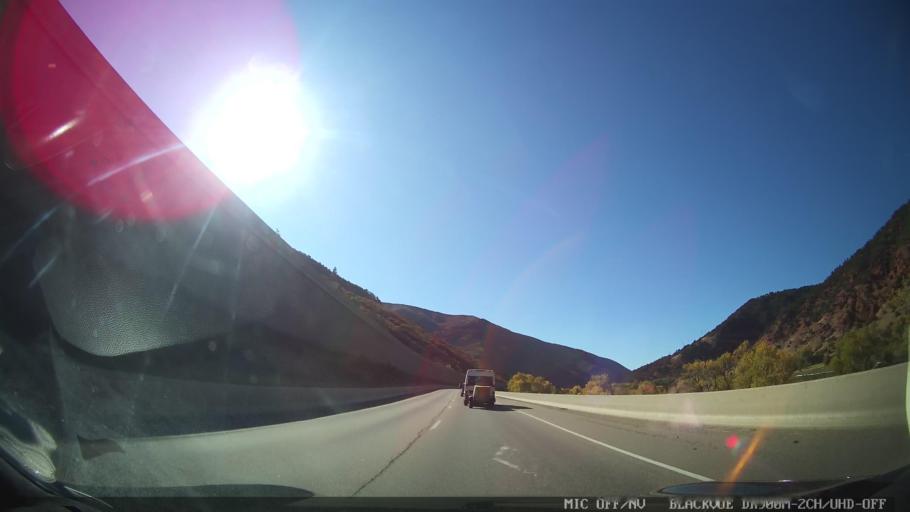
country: US
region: Colorado
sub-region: Eagle County
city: Basalt
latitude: 39.3300
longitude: -106.9729
